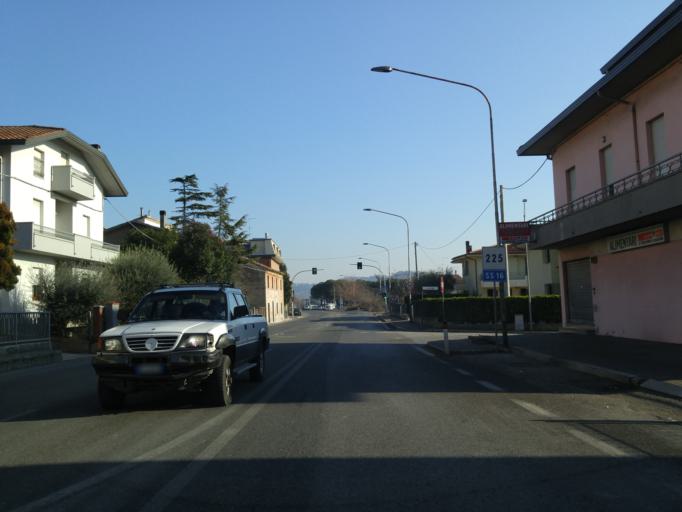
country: IT
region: The Marches
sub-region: Provincia di Pesaro e Urbino
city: Gabicce Mare
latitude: 43.9560
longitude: 12.7673
